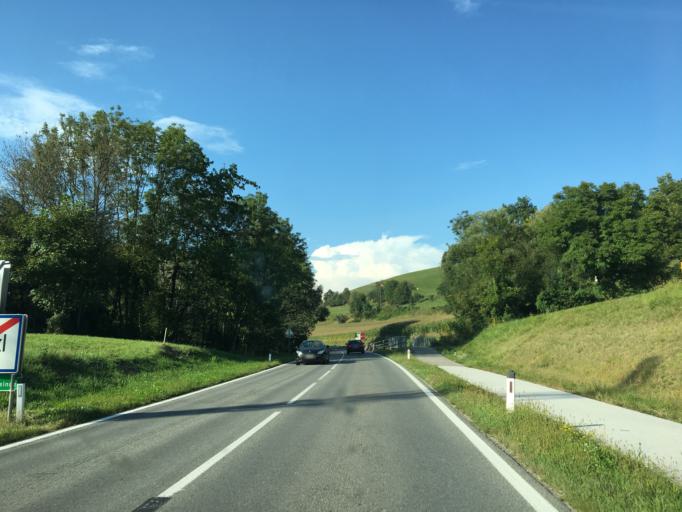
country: AT
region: Carinthia
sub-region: Politischer Bezirk Sankt Veit an der Glan
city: Bruckl
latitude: 46.7538
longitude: 14.5330
